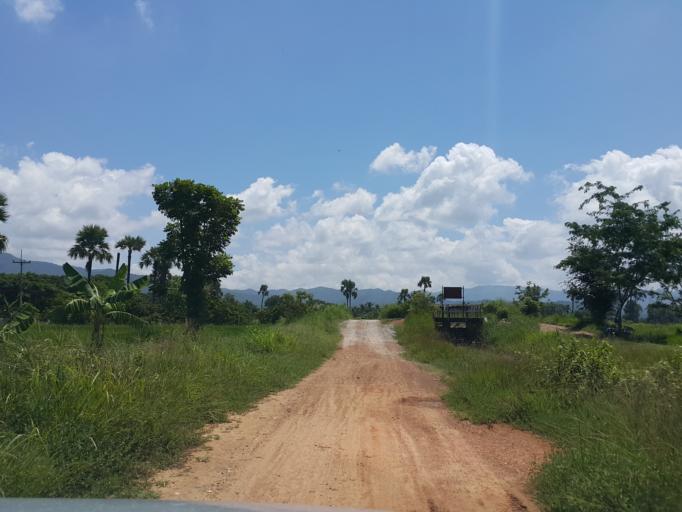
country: TH
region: Lamphun
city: Ban Thi
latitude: 18.6700
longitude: 99.1468
